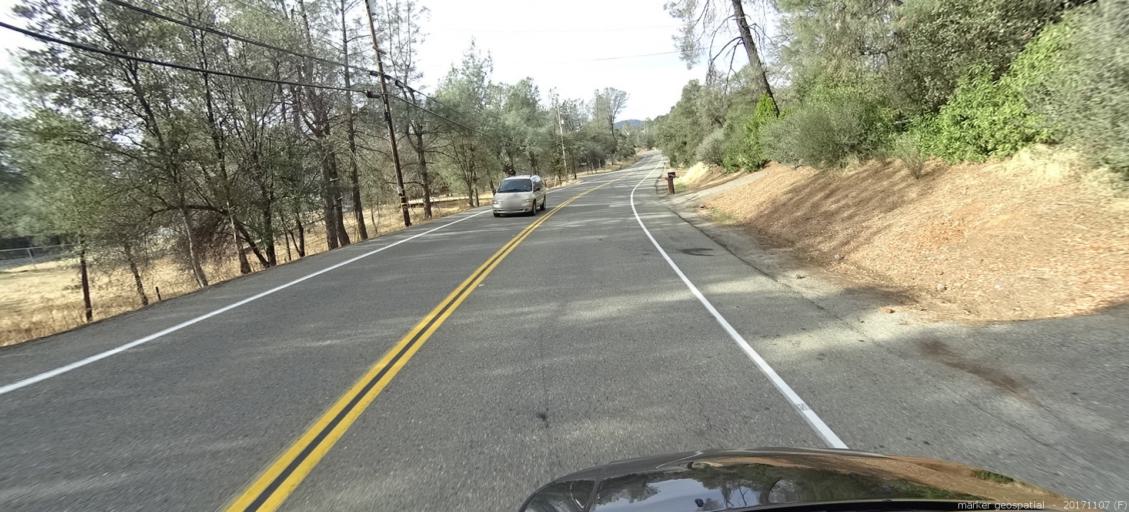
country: US
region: California
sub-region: Shasta County
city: Redding
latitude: 40.5530
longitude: -122.4462
